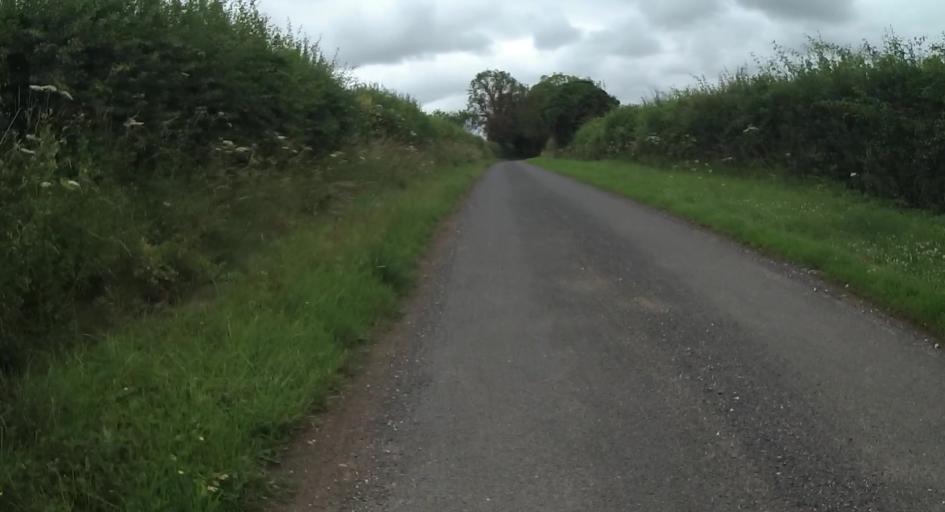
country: GB
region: England
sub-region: Hampshire
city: Four Marks
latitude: 51.0767
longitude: -1.1408
